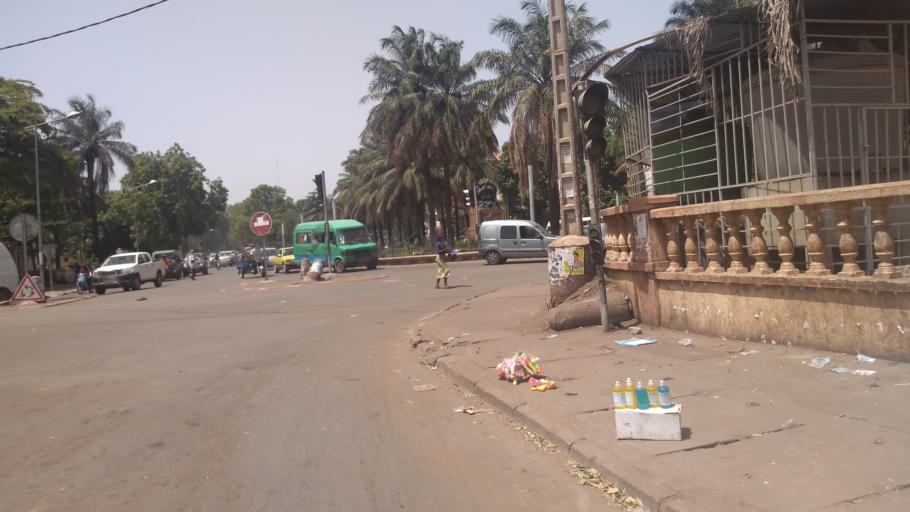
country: ML
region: Bamako
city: Bamako
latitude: 12.6460
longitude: -8.0017
